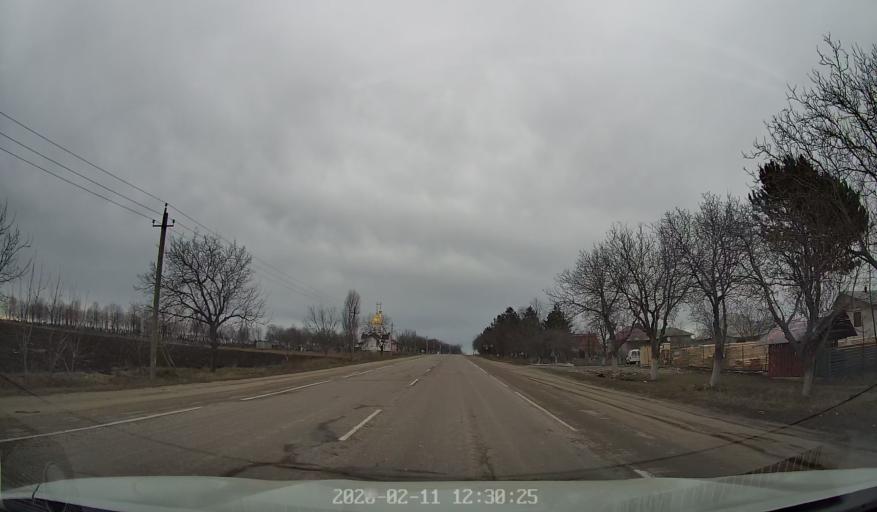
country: MD
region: Raionul Edinet
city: Edinet
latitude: 48.1634
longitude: 27.2833
